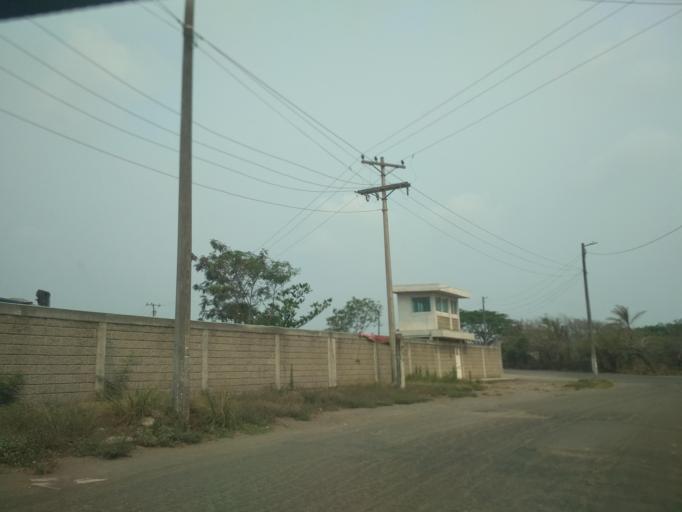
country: MX
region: Veracruz
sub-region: Veracruz
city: Delfino Victoria (Santa Fe)
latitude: 19.2099
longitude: -96.2577
